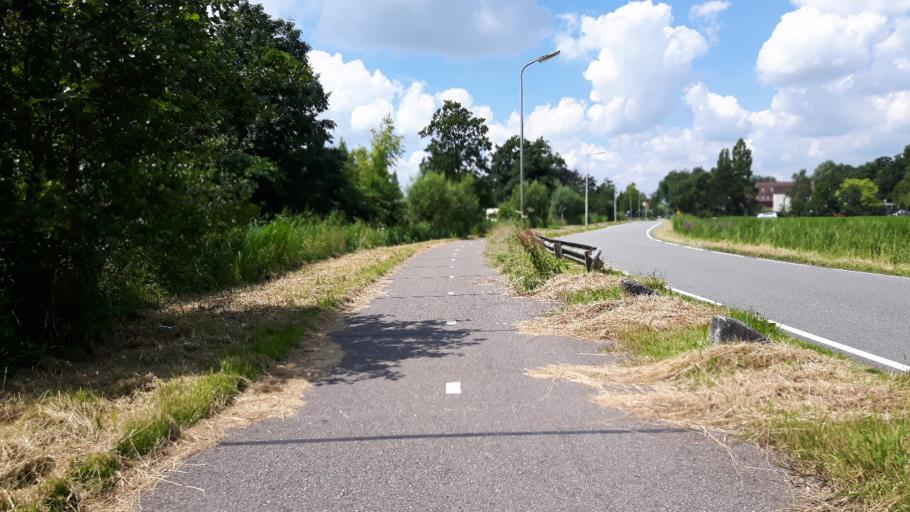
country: NL
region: South Holland
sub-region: Gemeente Gouda
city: Bloemendaal
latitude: 52.0439
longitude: 4.6802
